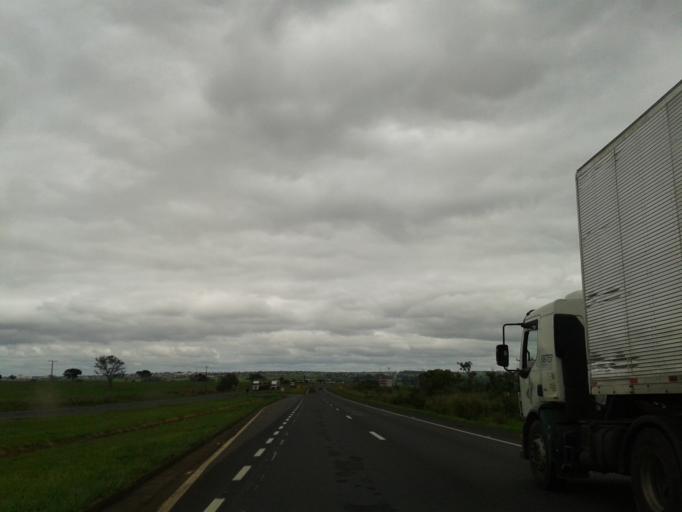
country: BR
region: Minas Gerais
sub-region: Uberlandia
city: Uberlandia
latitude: -19.0133
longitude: -48.2074
